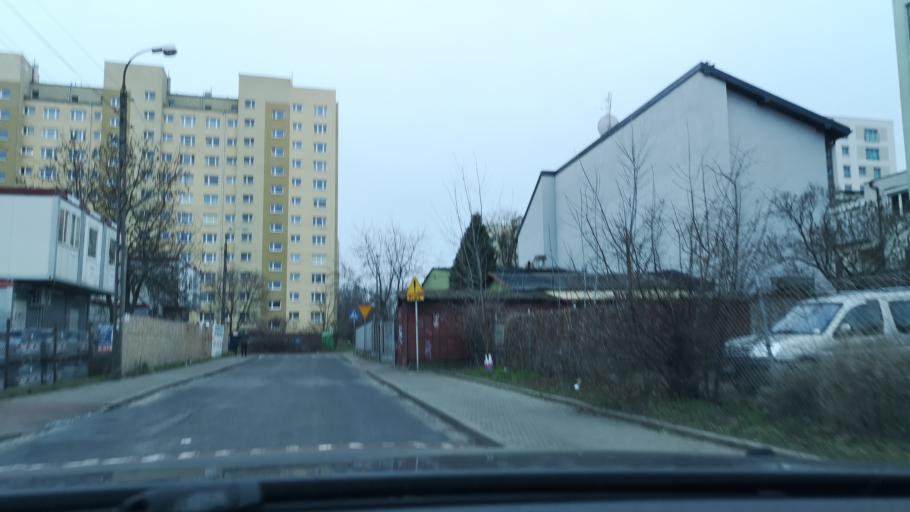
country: PL
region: Masovian Voivodeship
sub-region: Warszawa
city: Bemowo
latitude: 52.2425
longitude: 20.9210
